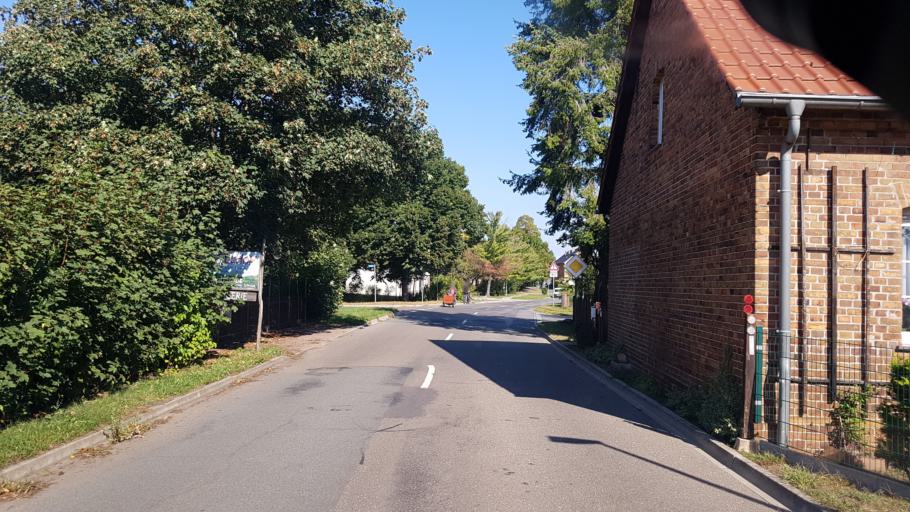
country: DE
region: Brandenburg
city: Vetschau
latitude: 51.7107
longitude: 14.0887
